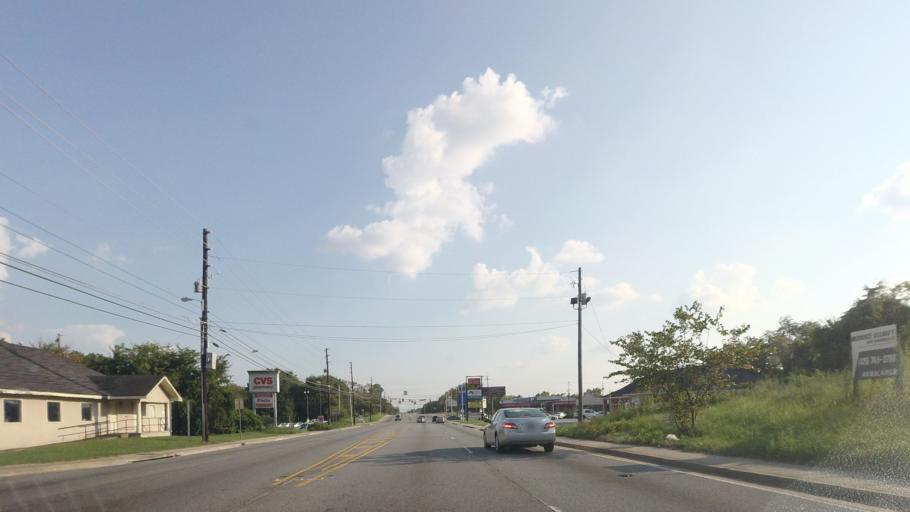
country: US
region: Georgia
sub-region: Bibb County
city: Macon
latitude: 32.8331
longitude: -83.6626
